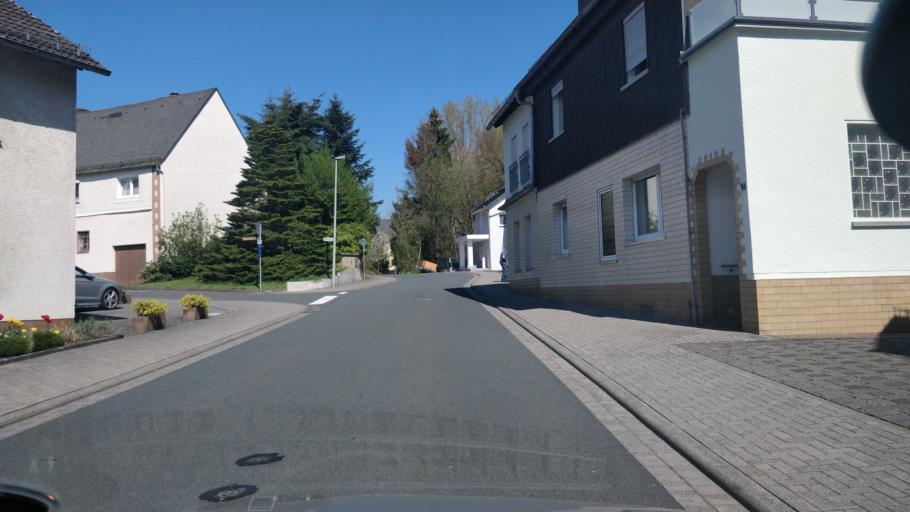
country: DE
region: Hesse
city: Waldbrunn
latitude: 50.5270
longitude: 8.0962
